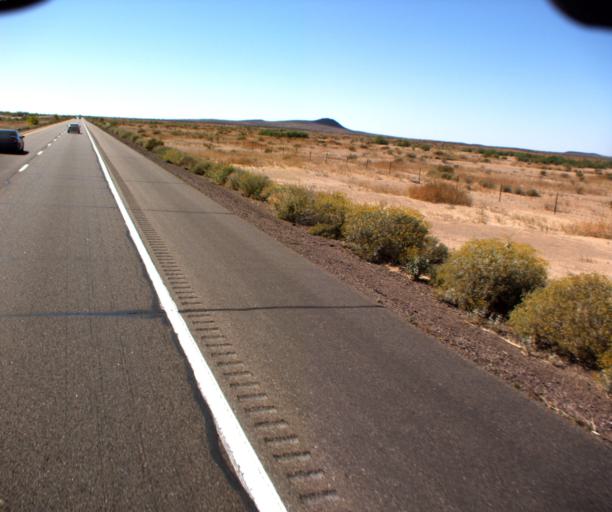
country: US
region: Arizona
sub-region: Maricopa County
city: Gila Bend
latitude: 32.8815
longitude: -113.1011
